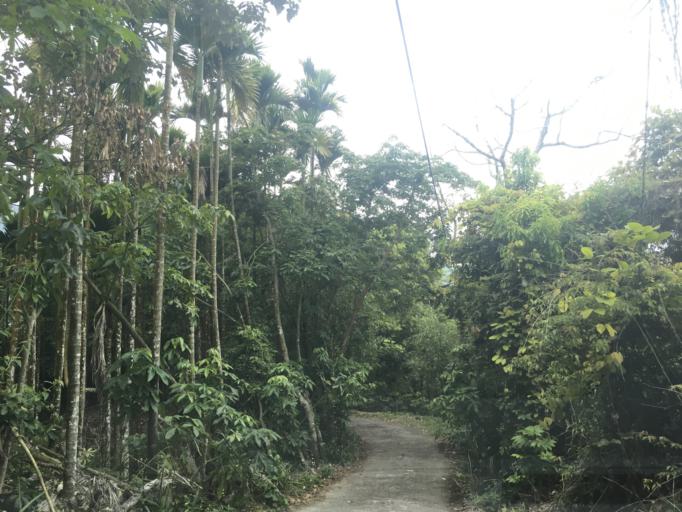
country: TW
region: Taiwan
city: Zhongxing New Village
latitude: 24.0473
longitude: 120.8018
